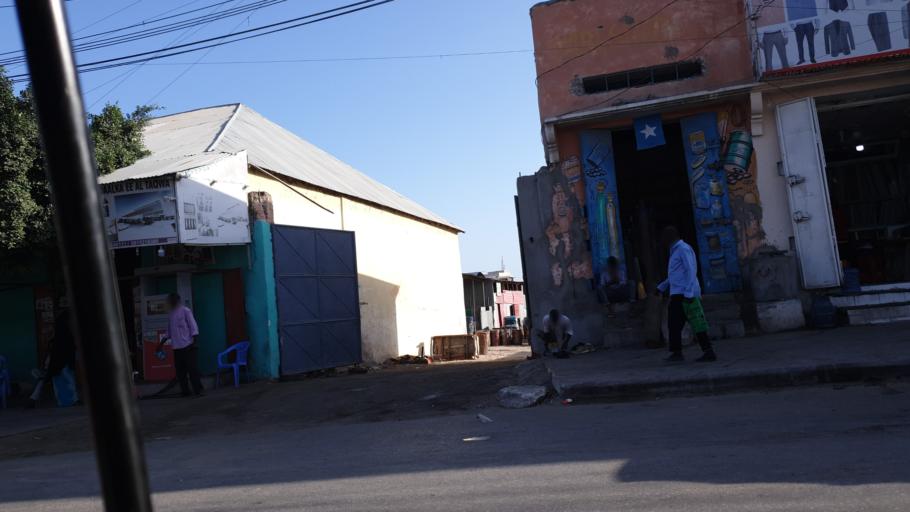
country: SO
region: Banaadir
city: Mogadishu
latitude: 2.0318
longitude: 45.3066
